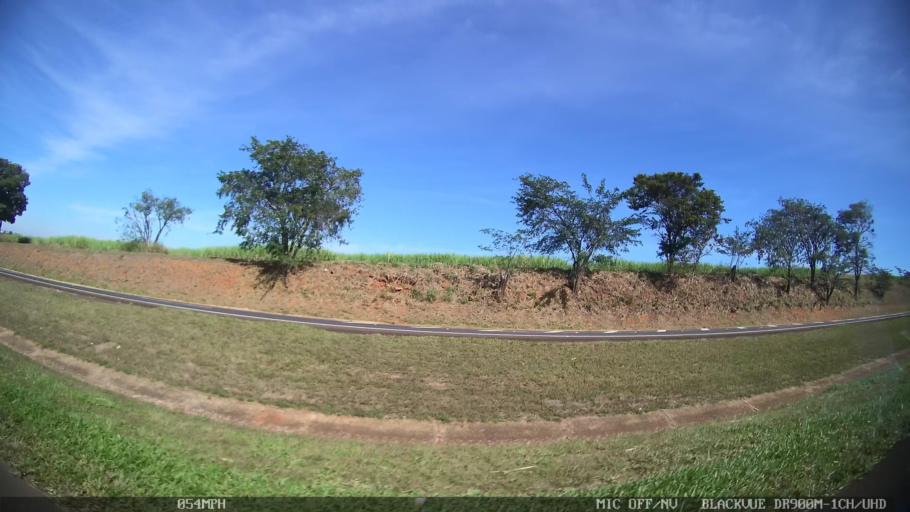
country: BR
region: Sao Paulo
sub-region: Porto Ferreira
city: Porto Ferreira
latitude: -21.8002
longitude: -47.5075
